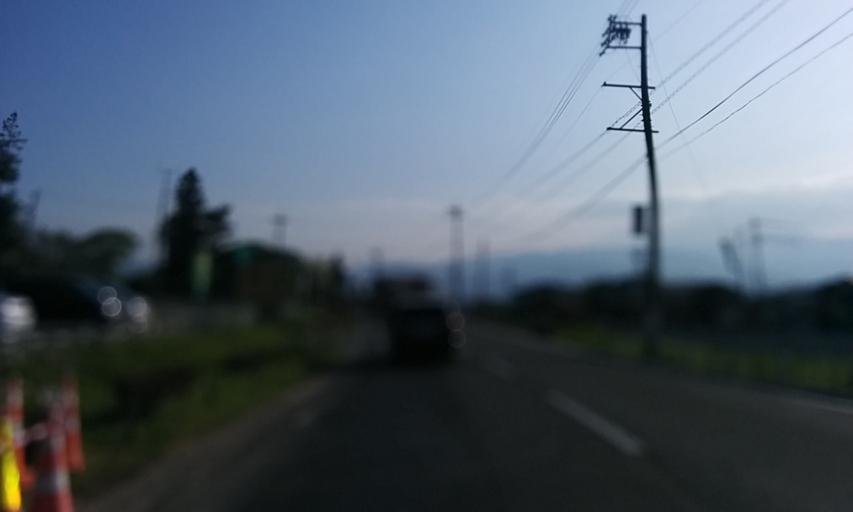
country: JP
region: Nagano
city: Matsumoto
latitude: 36.1716
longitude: 137.9976
